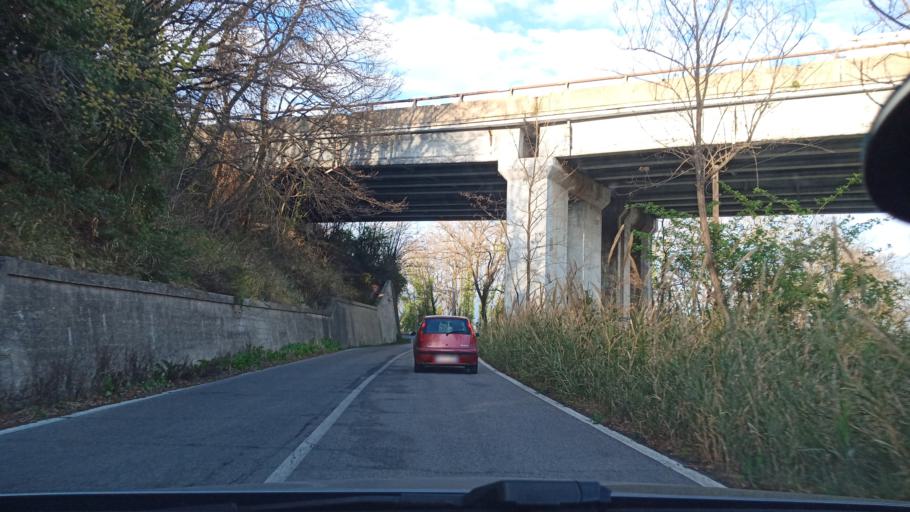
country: IT
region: Latium
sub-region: Citta metropolitana di Roma Capitale
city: Nazzano
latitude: 42.2128
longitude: 12.6003
